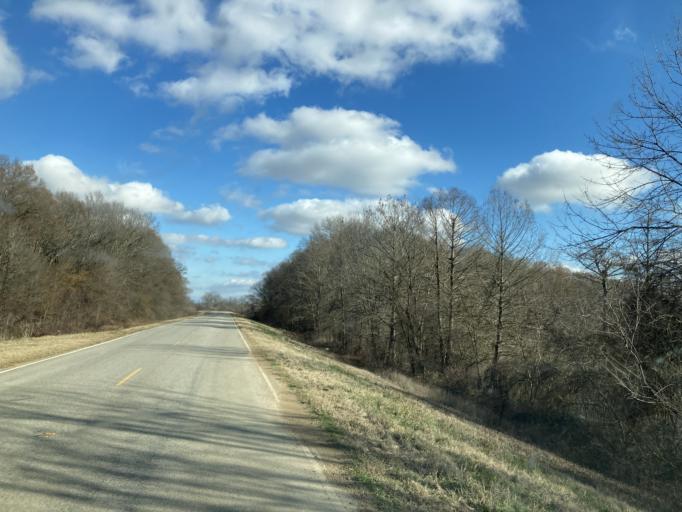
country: US
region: Mississippi
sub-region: Yazoo County
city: Yazoo City
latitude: 32.9653
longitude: -90.4619
